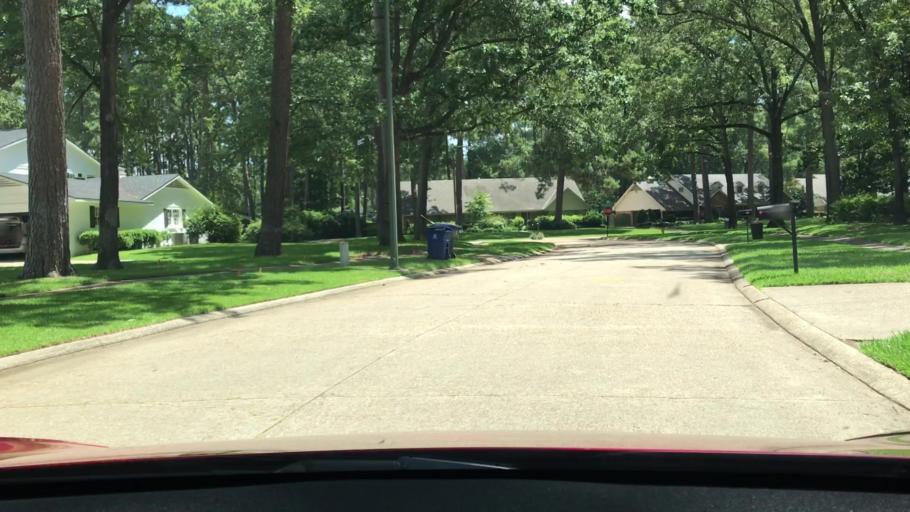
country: US
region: Louisiana
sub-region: Bossier Parish
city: Bossier City
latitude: 32.4293
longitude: -93.7383
